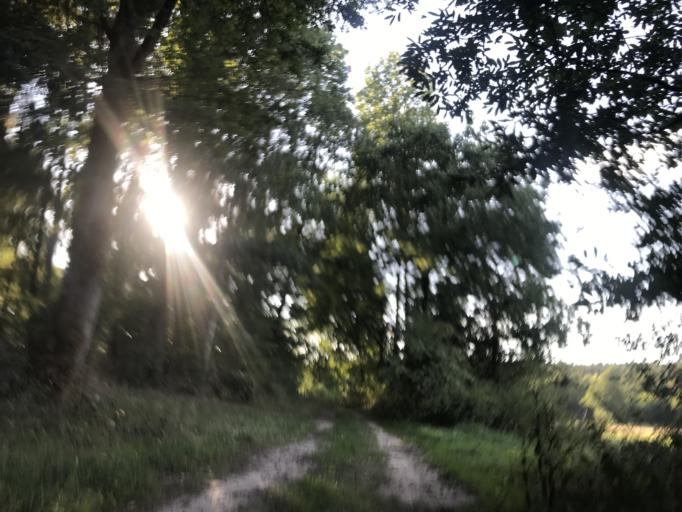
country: DE
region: Lower Saxony
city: Neetze
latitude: 53.2431
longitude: 10.6143
